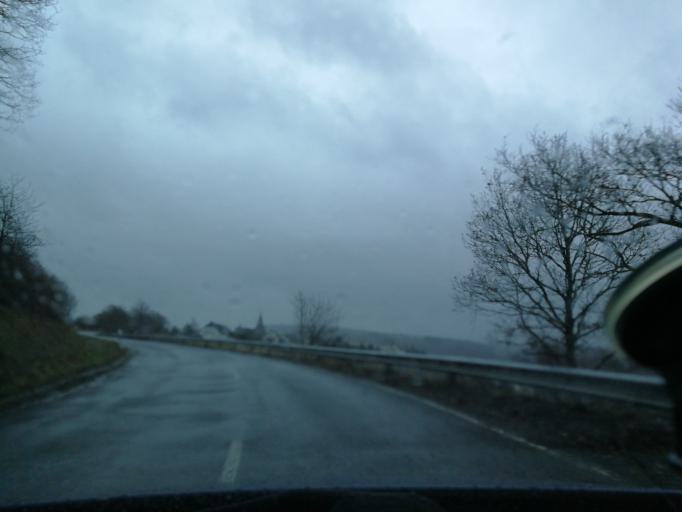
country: DE
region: Rheinland-Pfalz
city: Berglicht
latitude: 49.7915
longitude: 6.9648
